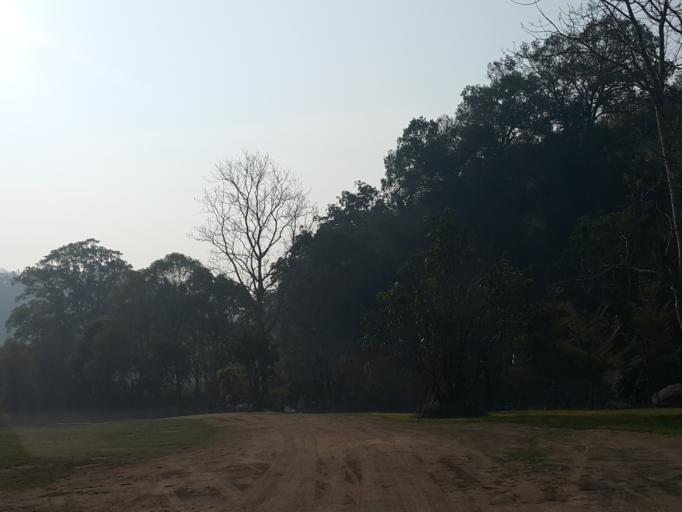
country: TH
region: Chiang Mai
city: Hang Dong
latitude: 18.7602
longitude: 98.8748
